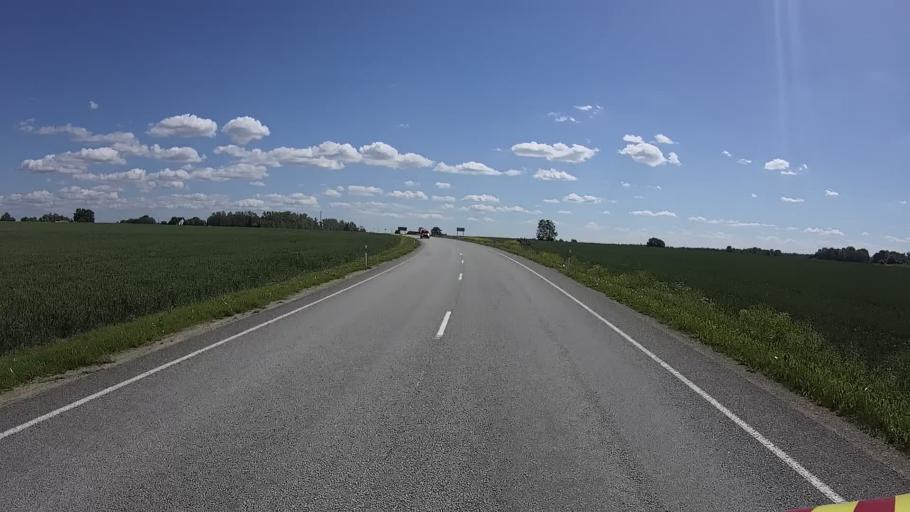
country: EE
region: Ida-Virumaa
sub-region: Johvi vald
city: Johvi
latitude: 59.3734
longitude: 27.3490
